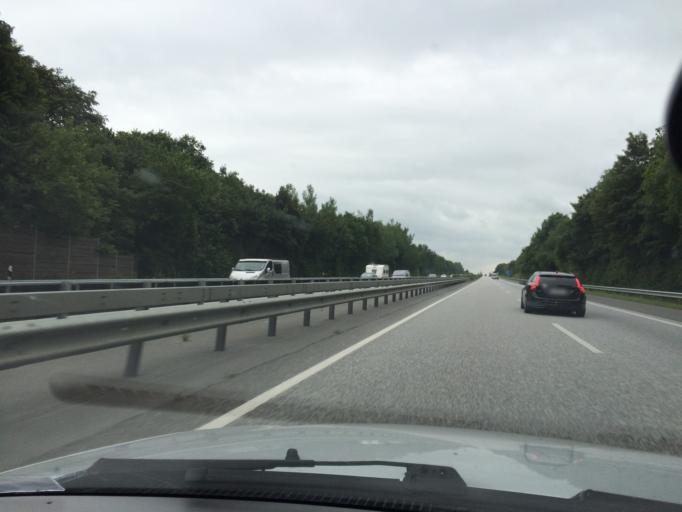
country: DE
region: Schleswig-Holstein
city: Jarplund-Weding
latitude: 54.7488
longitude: 9.3758
